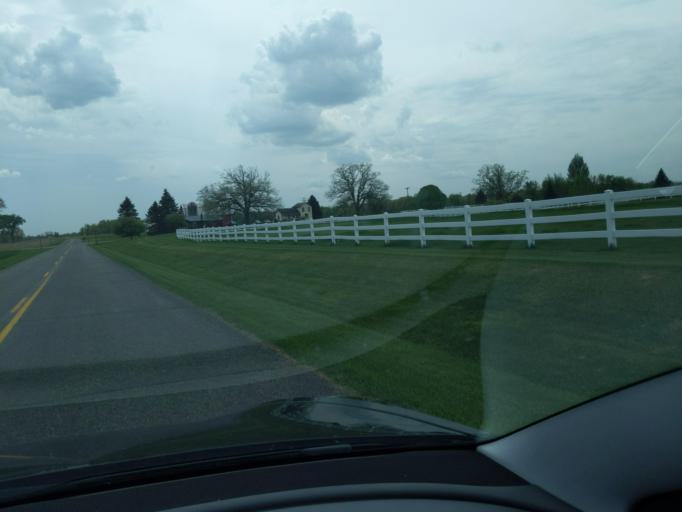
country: US
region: Michigan
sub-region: Ingham County
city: Leslie
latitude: 42.4911
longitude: -84.3318
